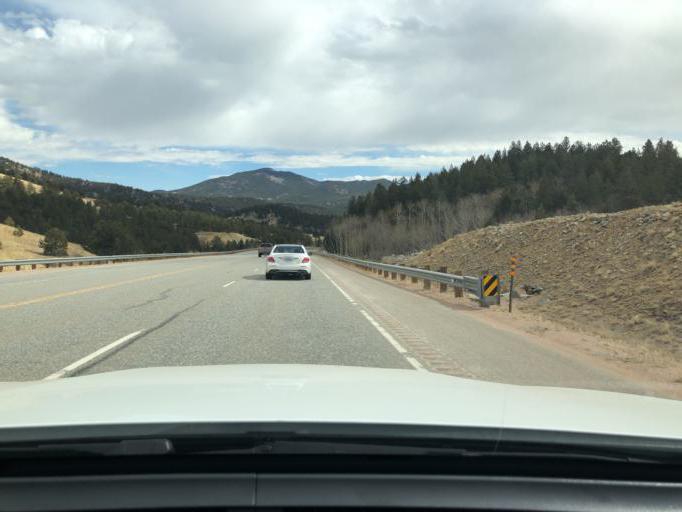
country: US
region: Colorado
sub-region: Gilpin County
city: Central City
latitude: 39.7857
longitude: -105.4906
